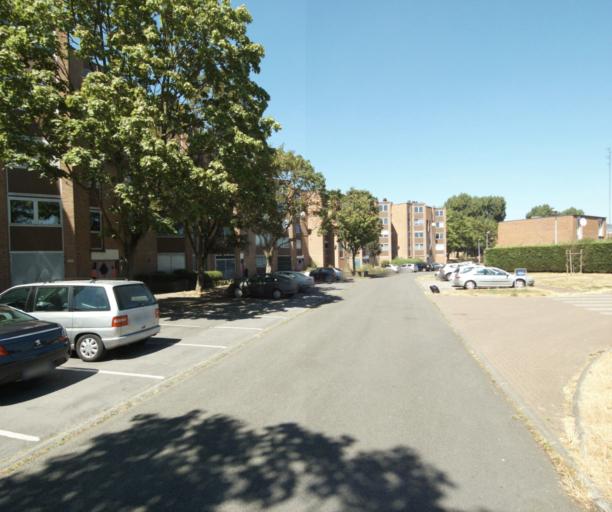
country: BE
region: Wallonia
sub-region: Province du Hainaut
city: Mouscron
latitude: 50.7381
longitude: 3.1830
